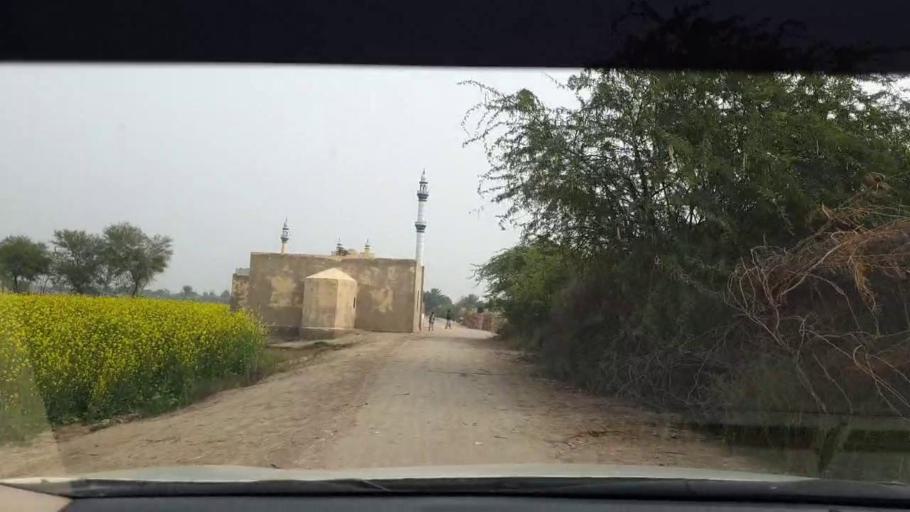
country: PK
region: Sindh
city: Berani
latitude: 25.8381
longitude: 68.8494
